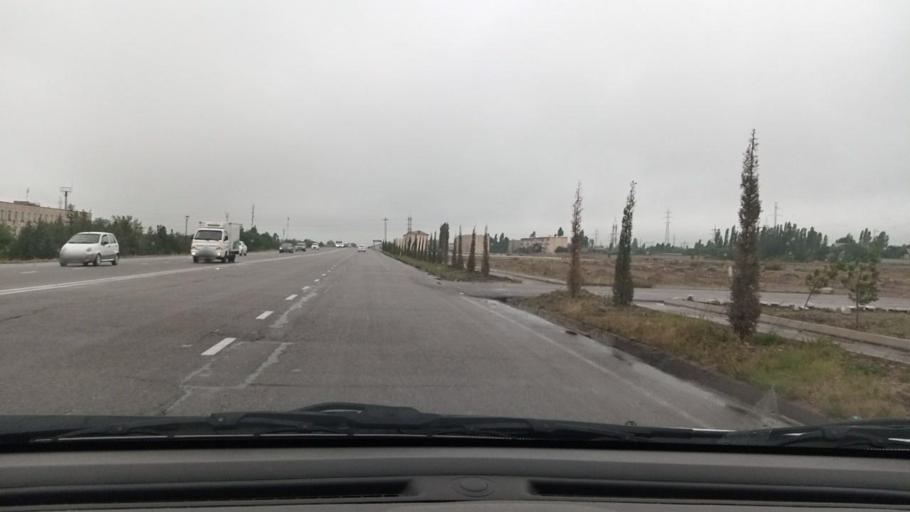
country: UZ
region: Toshkent
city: Angren
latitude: 41.0166
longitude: 70.1119
